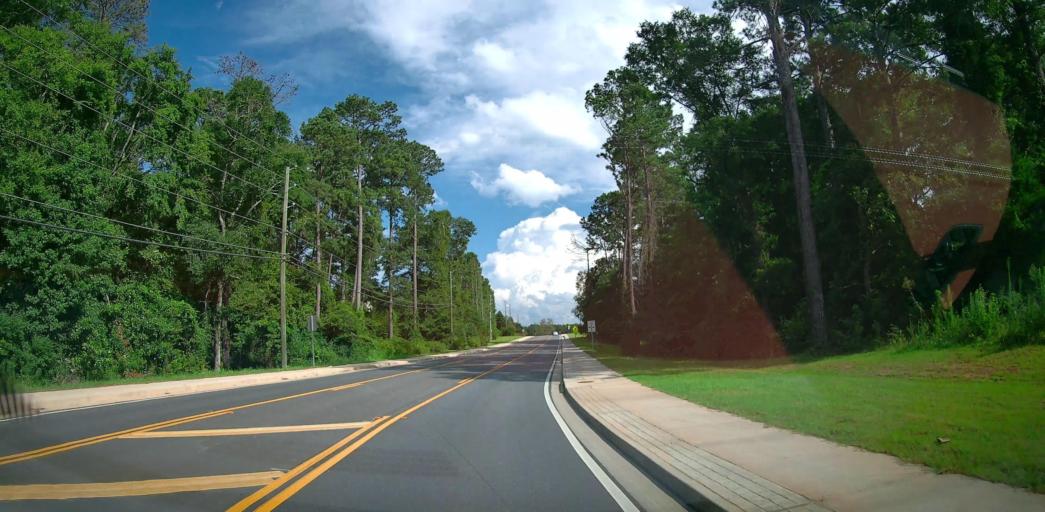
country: US
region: Georgia
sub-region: Houston County
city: Robins Air Force Base
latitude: 32.5420
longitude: -83.5725
